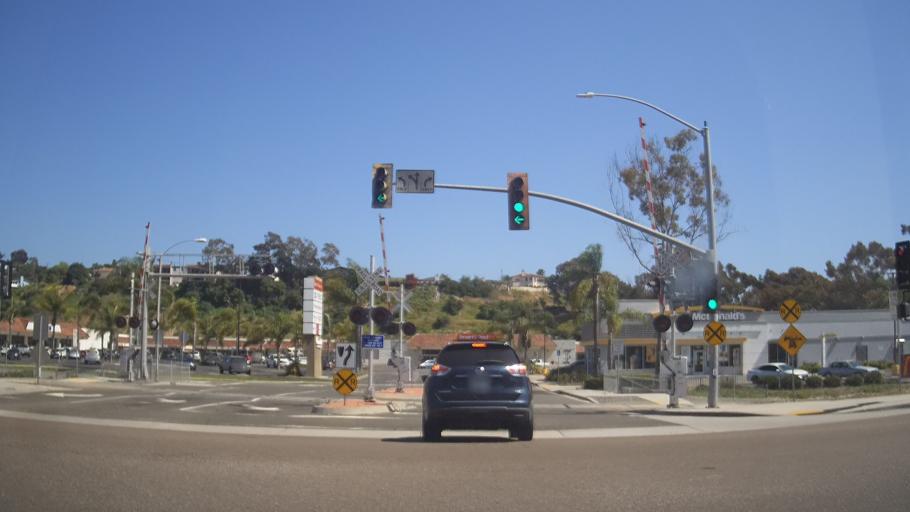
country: US
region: California
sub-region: San Diego County
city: Oceanside
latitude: 33.1911
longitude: -117.3613
